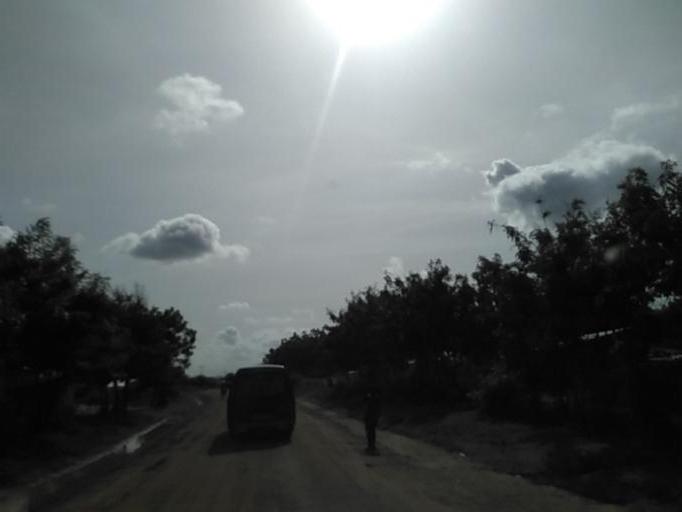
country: GH
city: Akropong
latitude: 6.0319
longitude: 0.3397
